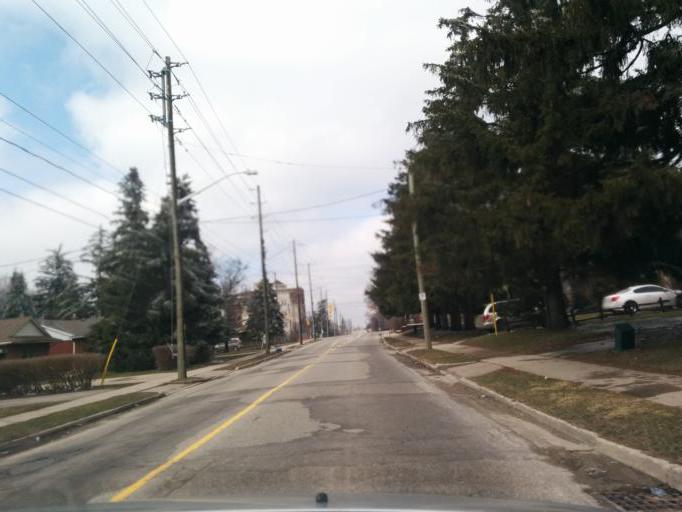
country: CA
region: Ontario
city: Waterloo
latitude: 43.4776
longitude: -80.5345
